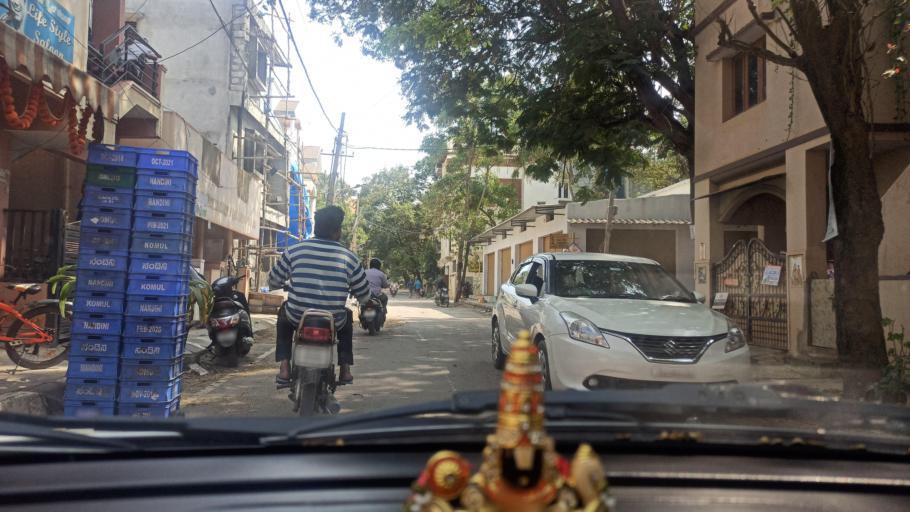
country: IN
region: Karnataka
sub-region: Bangalore Urban
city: Bangalore
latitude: 13.0224
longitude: 77.6586
